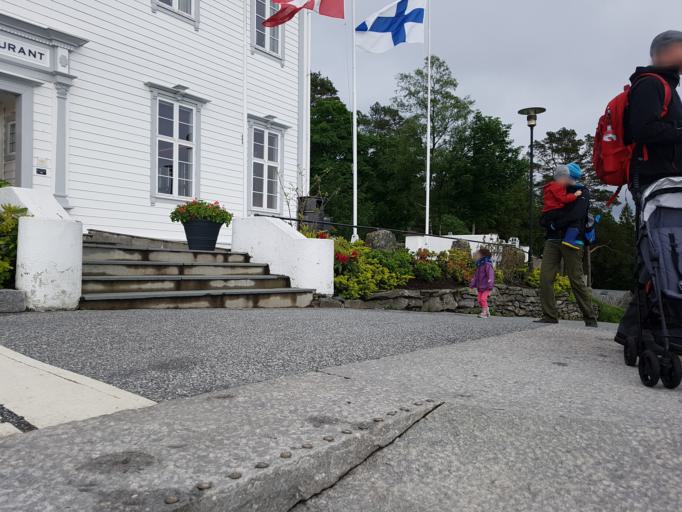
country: NO
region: Hordaland
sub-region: Bergen
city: Bergen
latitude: 60.3941
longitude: 5.3437
